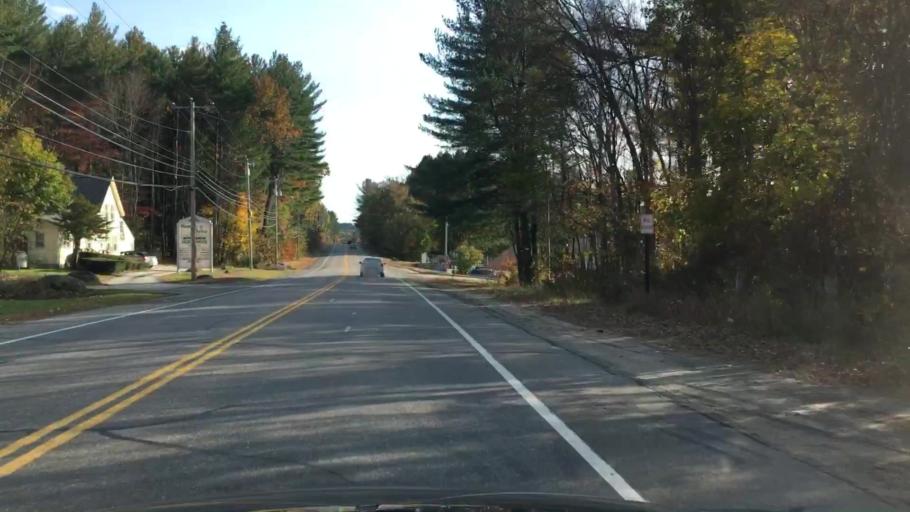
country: US
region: New Hampshire
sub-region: Hillsborough County
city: Milford
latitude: 42.8261
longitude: -71.6477
